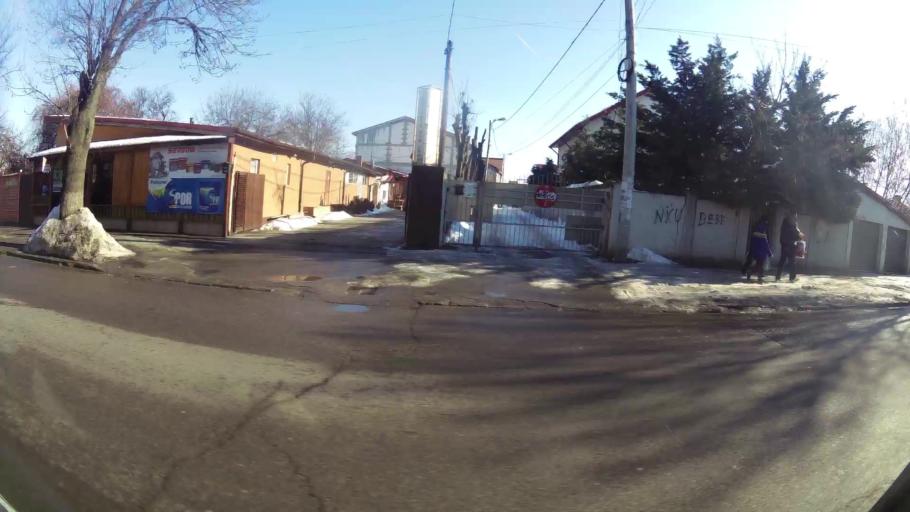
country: RO
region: Ilfov
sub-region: Comuna Magurele
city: Magurele
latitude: 44.3973
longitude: 26.0486
